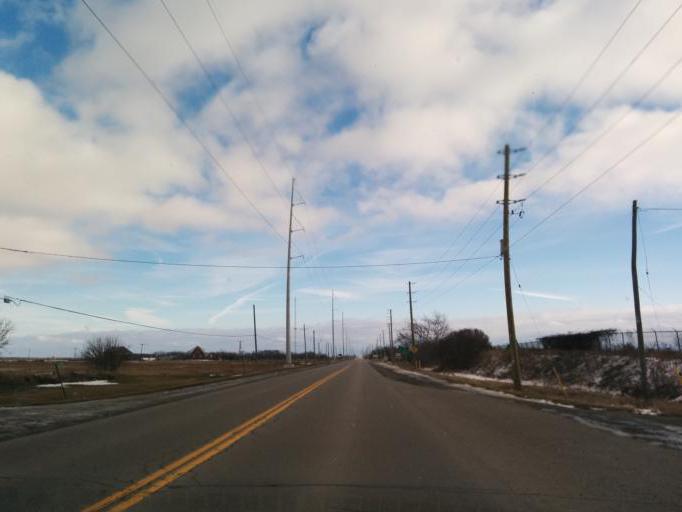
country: CA
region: Ontario
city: Ancaster
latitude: 42.9510
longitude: -80.0211
